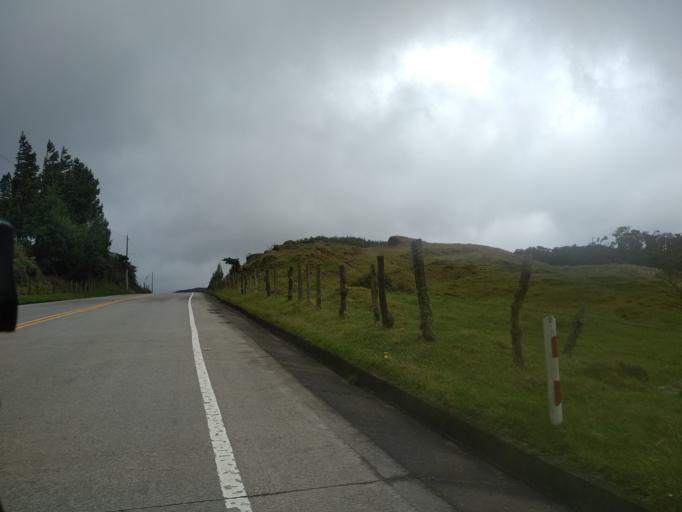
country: EC
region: Loja
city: Loja
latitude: -3.8848
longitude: -79.2632
